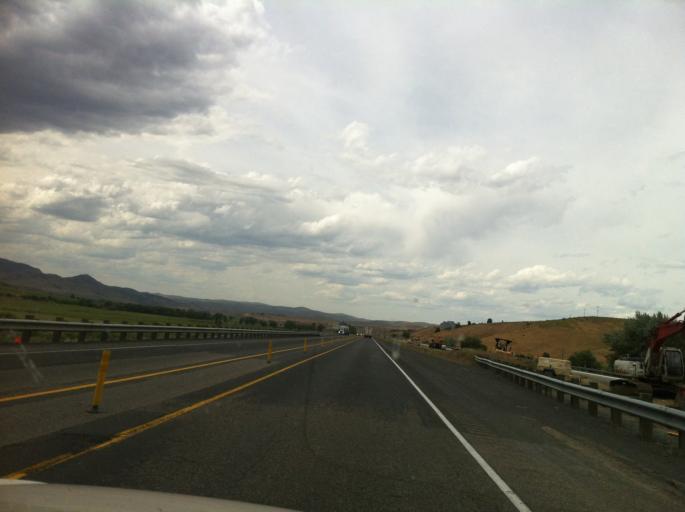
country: US
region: Oregon
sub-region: Baker County
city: Baker City
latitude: 44.5467
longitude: -117.4204
